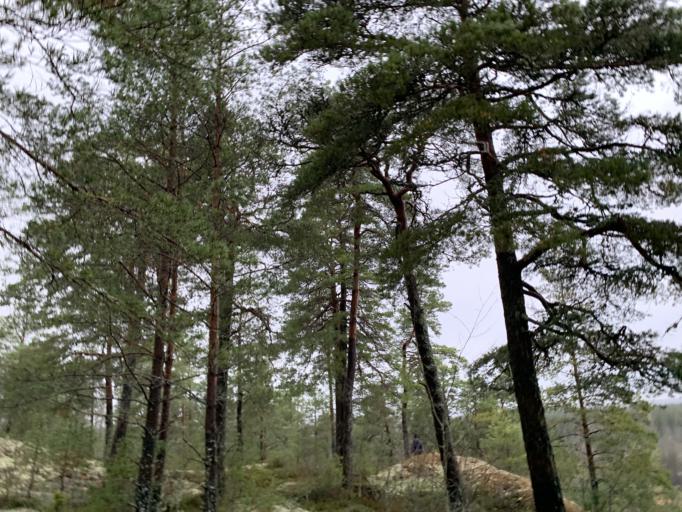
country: SE
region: Soedermanland
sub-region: Eskilstuna Kommun
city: Kvicksund
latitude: 59.3690
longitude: 16.2872
